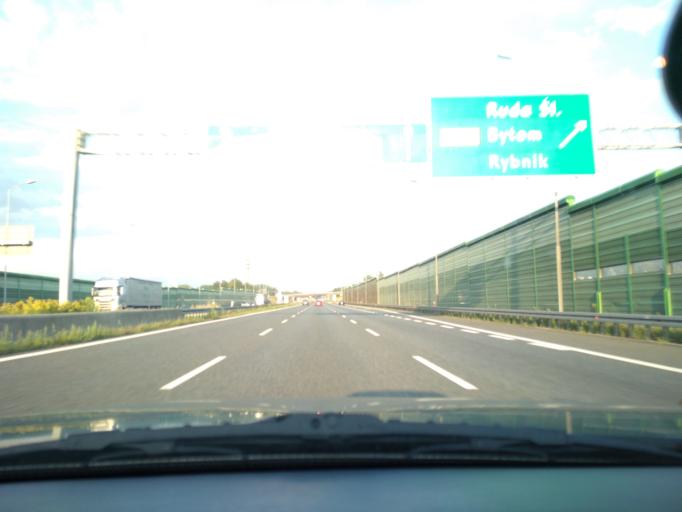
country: PL
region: Silesian Voivodeship
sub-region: Ruda Slaska
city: Ruda Slaska
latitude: 50.2569
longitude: 18.8464
